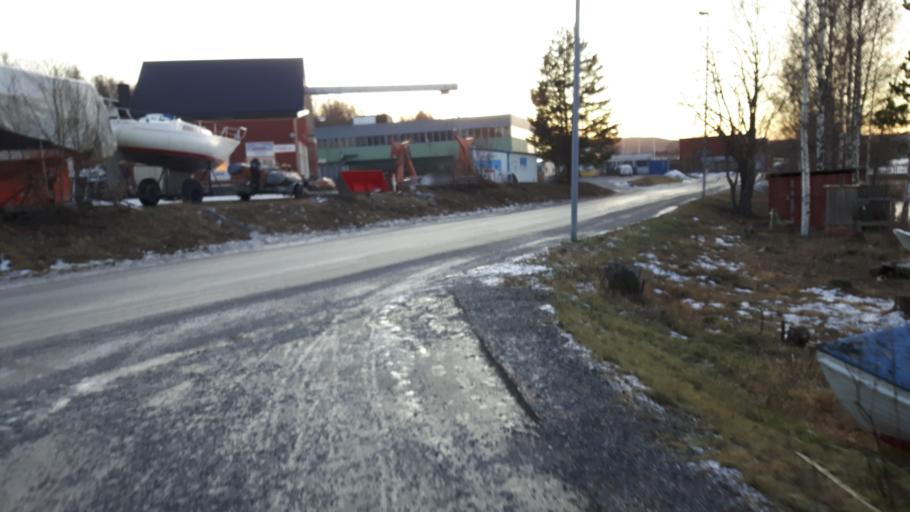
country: SE
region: Vaesternorrland
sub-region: Haernoesands Kommun
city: Haernoesand
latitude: 62.6234
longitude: 17.9464
